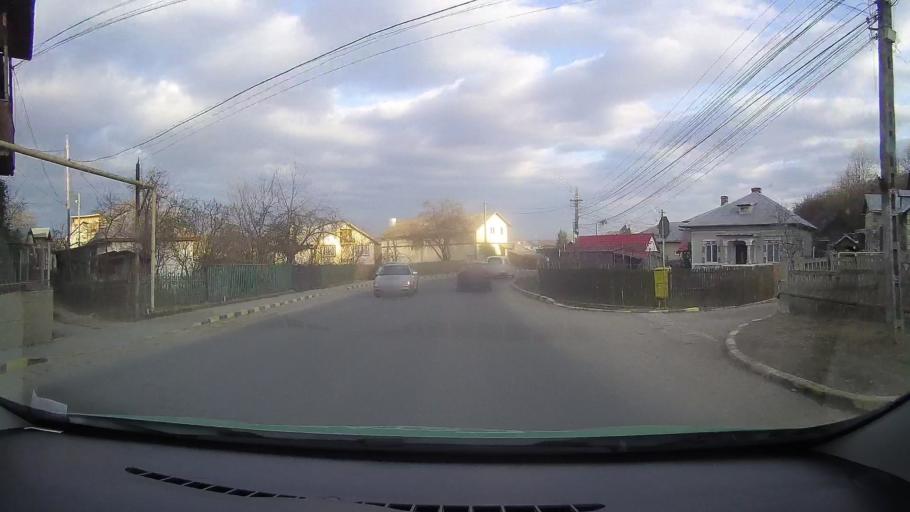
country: RO
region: Dambovita
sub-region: Municipiul Moreni
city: Moreni
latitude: 44.9811
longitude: 25.6336
